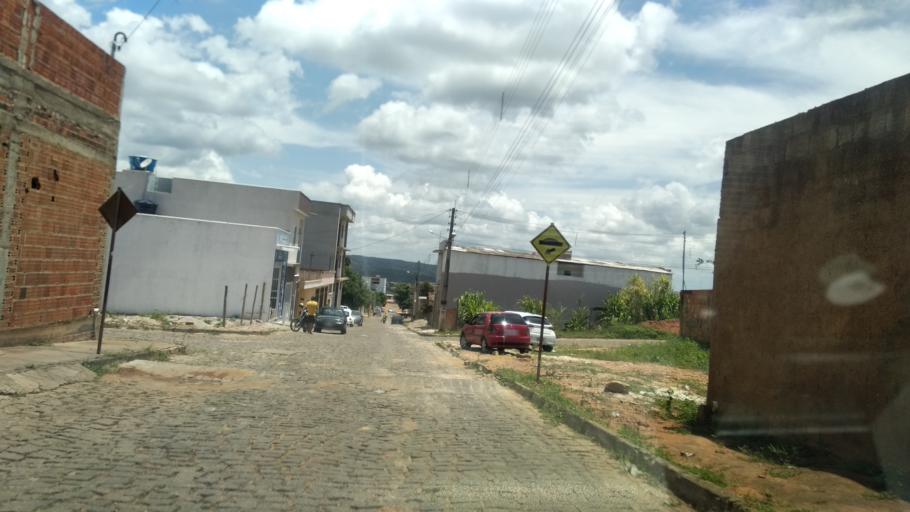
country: BR
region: Bahia
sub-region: Caetite
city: Caetite
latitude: -14.0615
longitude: -42.4872
